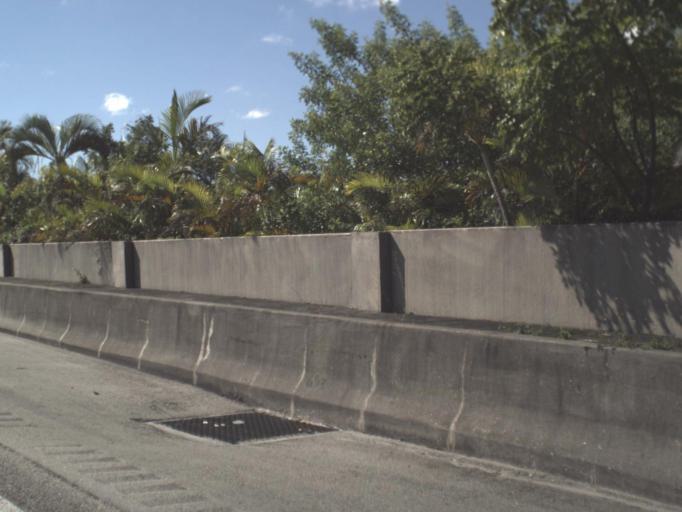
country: US
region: Florida
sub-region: Miami-Dade County
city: Westwood Lake
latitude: 25.7161
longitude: -80.3838
